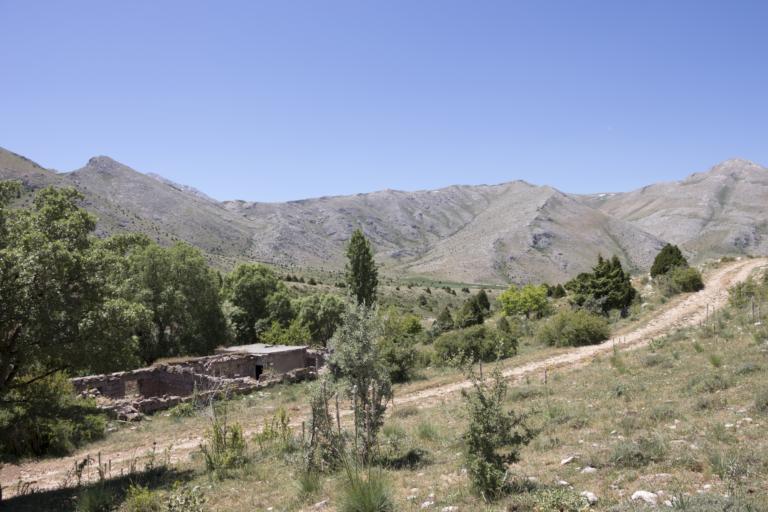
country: TR
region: Kayseri
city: Toklar
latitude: 38.4054
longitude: 36.1253
